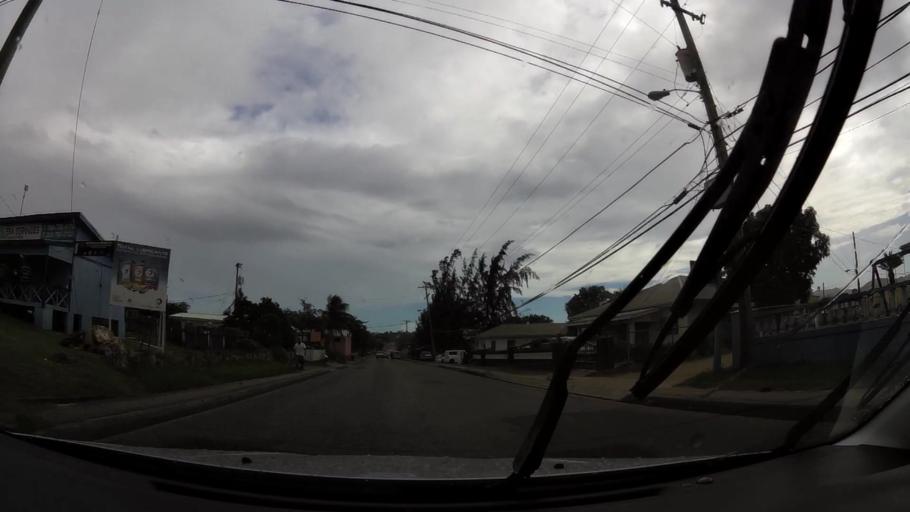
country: AG
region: Saint John
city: Saint John's
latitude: 17.1063
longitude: -61.8339
